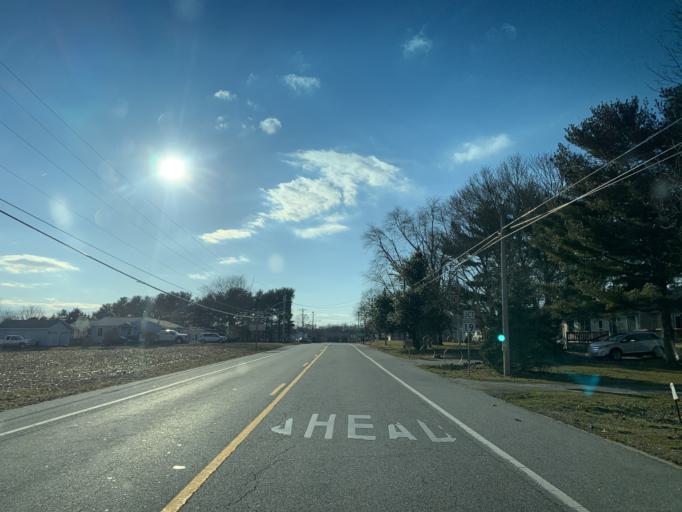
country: US
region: Maryland
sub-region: Queen Anne's County
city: Kingstown
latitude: 39.1488
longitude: -75.9761
